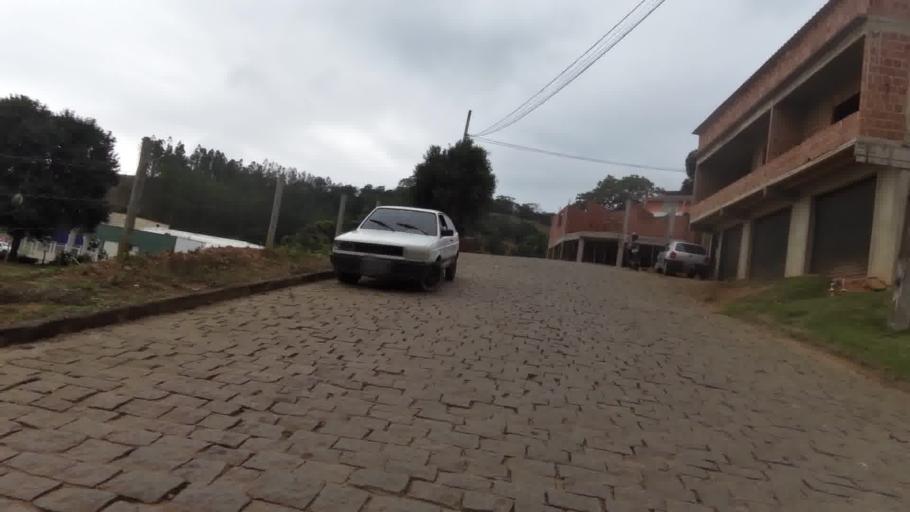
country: BR
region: Espirito Santo
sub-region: Alfredo Chaves
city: Alfredo Chaves
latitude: -20.6399
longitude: -40.7480
